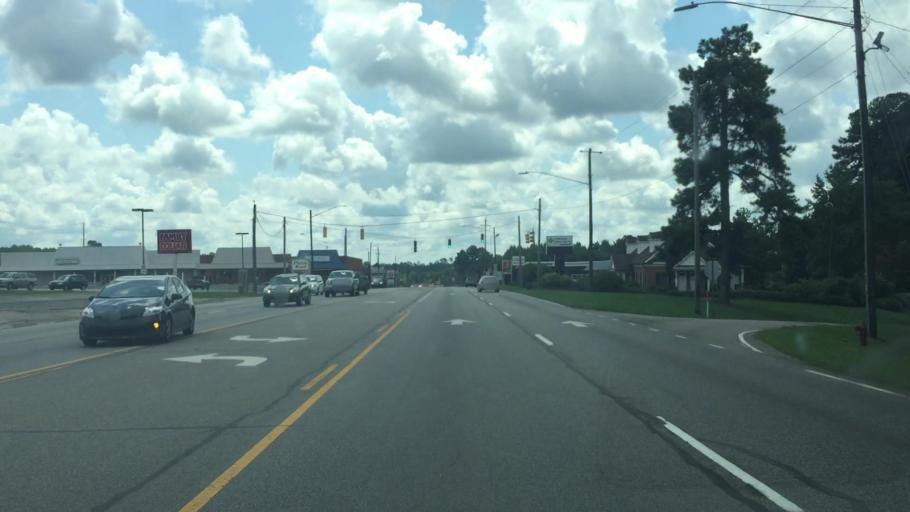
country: US
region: North Carolina
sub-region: Anson County
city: Wadesboro
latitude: 34.9676
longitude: -80.0640
